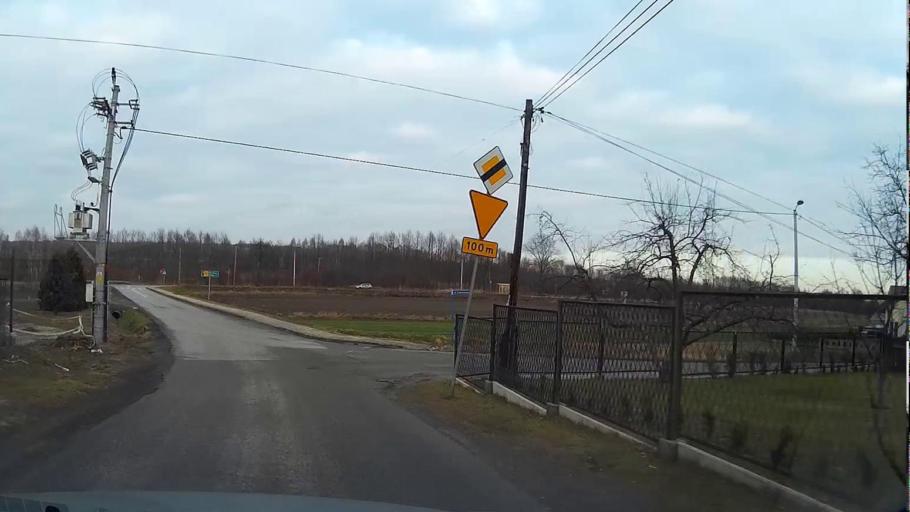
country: PL
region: Lesser Poland Voivodeship
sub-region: Powiat chrzanowski
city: Kwaczala
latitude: 50.0650
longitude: 19.4790
